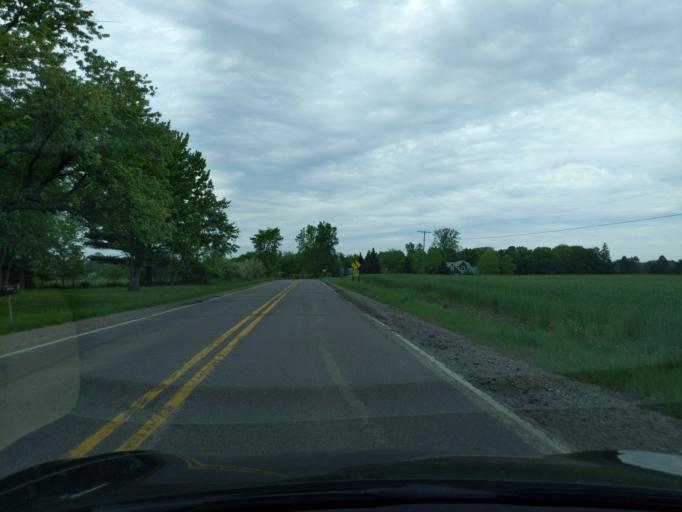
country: US
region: Michigan
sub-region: Ingham County
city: Mason
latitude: 42.6151
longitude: -84.3584
